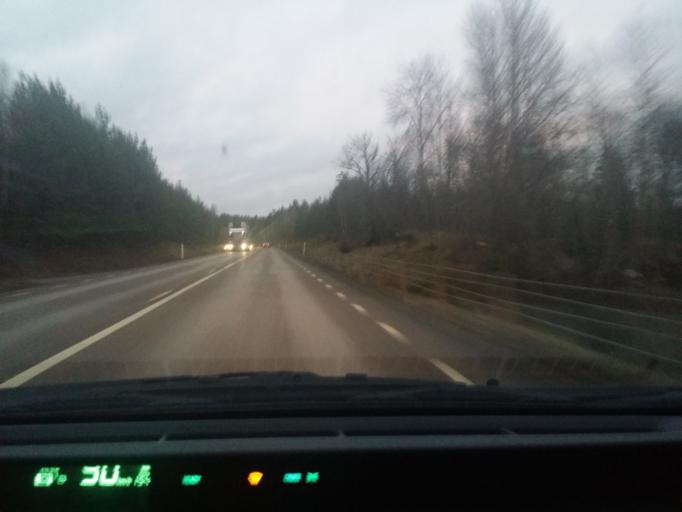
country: SE
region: Soedermanland
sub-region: Eskilstuna Kommun
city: Kvicksund
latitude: 59.5144
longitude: 16.3181
